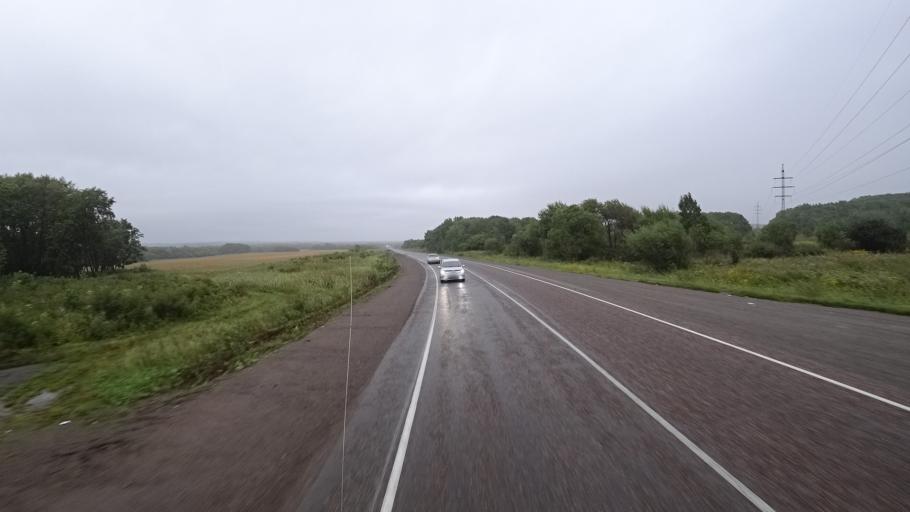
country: RU
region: Primorskiy
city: Monastyrishche
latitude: 44.2773
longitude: 132.4871
